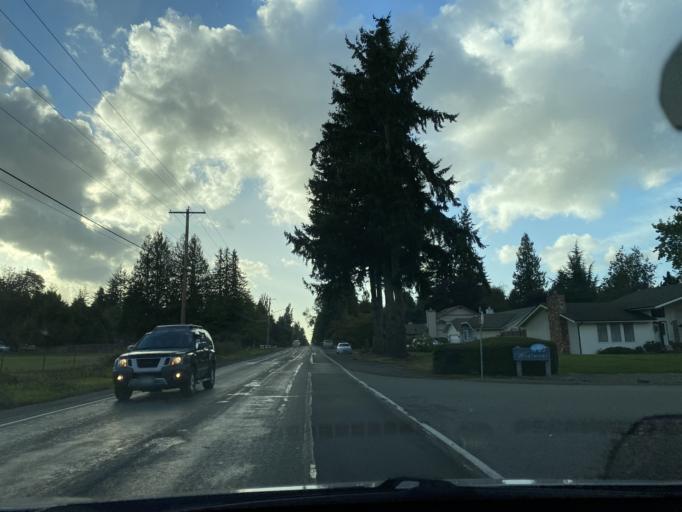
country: US
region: Washington
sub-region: Pierce County
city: South Hill
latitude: 47.1184
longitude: -122.2777
